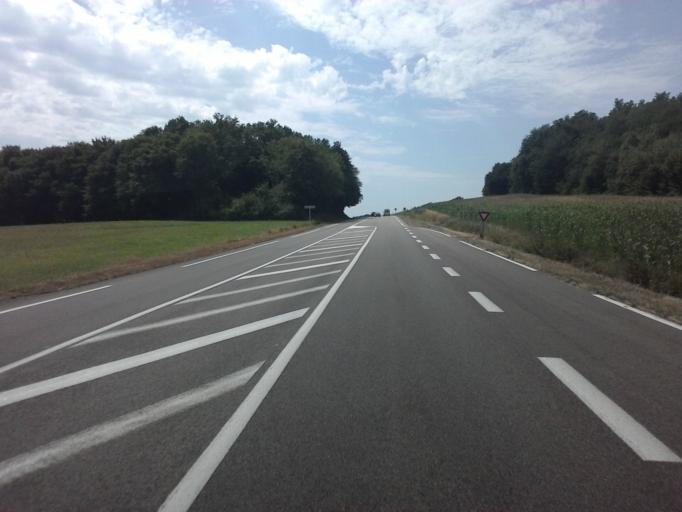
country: FR
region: Rhone-Alpes
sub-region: Departement de l'Ain
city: Saint-Etienne-du-Bois
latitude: 46.3150
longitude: 5.3054
